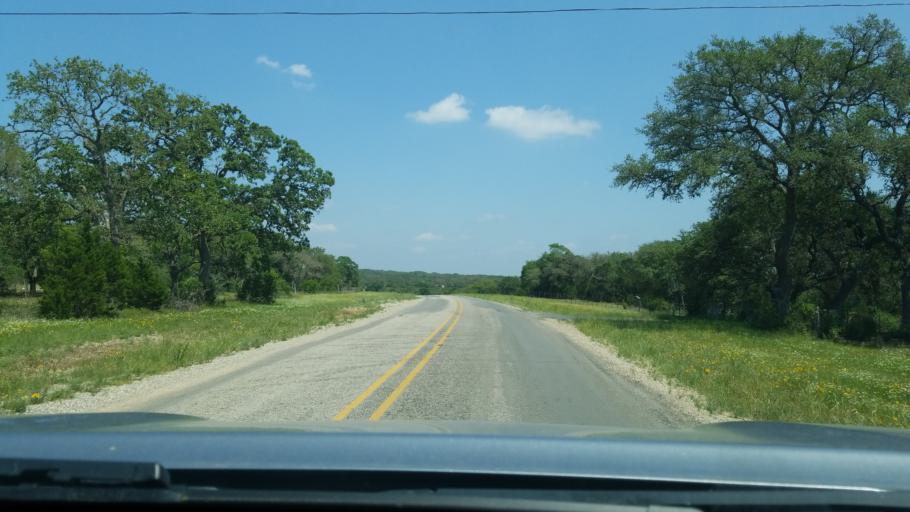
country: US
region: Texas
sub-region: Blanco County
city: Blanco
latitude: 29.9738
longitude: -98.5338
